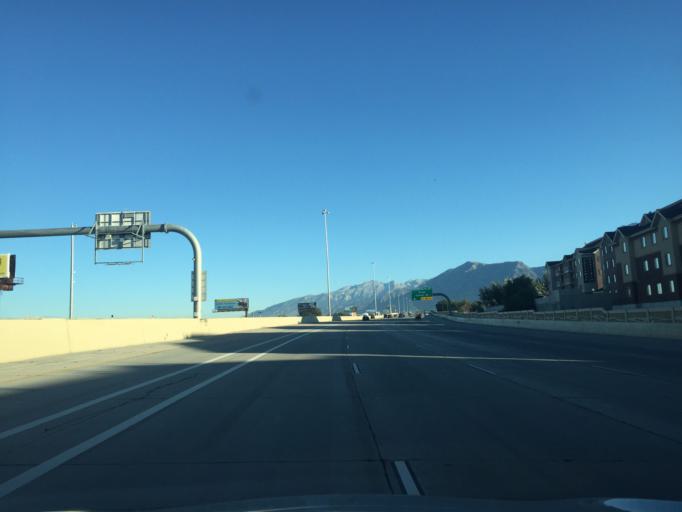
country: US
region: Utah
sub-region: Utah County
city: Orem
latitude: 40.2844
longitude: -111.7252
